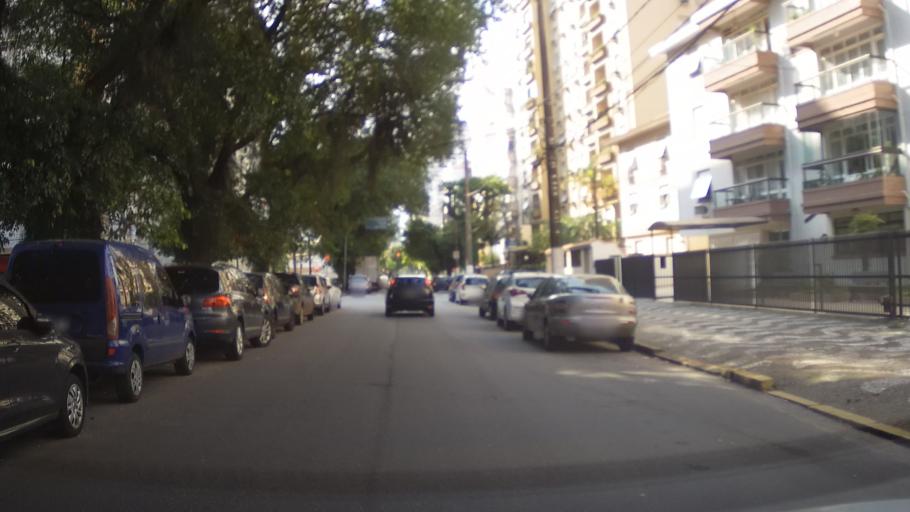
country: BR
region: Sao Paulo
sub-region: Santos
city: Santos
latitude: -23.9839
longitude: -46.3067
